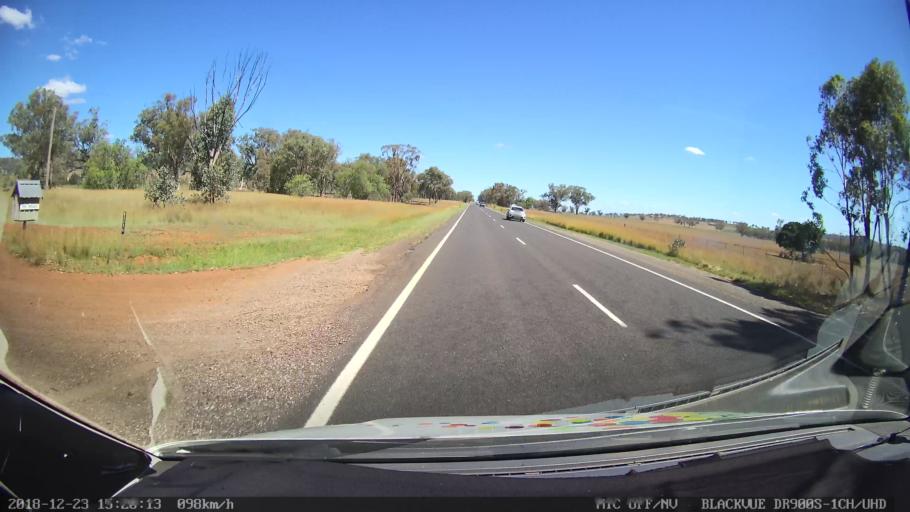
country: AU
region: New South Wales
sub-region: Tamworth Municipality
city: Manilla
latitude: -30.8397
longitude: 150.7882
